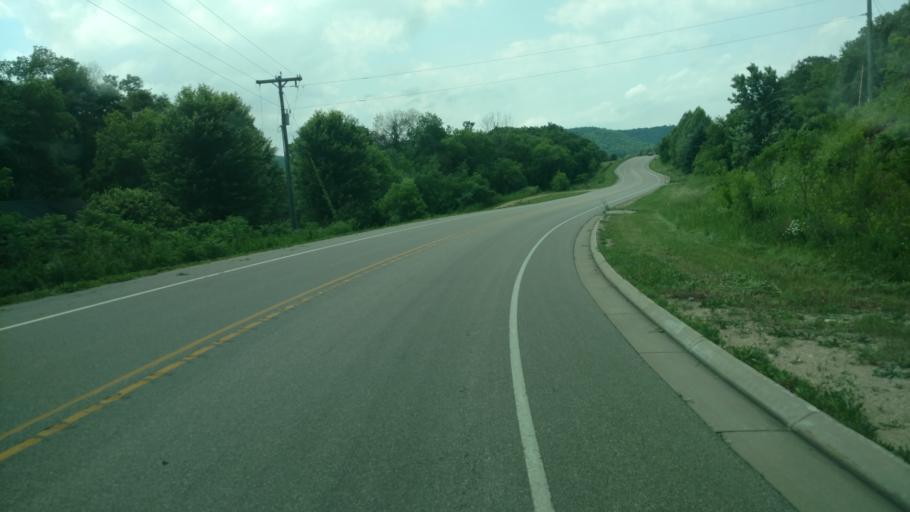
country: US
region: Wisconsin
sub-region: Vernon County
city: Viroqua
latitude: 43.4664
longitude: -90.7264
